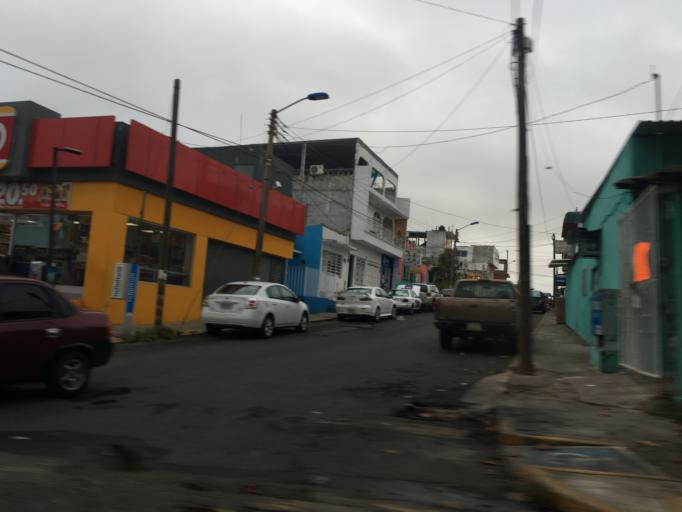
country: MX
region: Tabasco
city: Villahermosa
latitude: 17.9847
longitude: -92.9510
